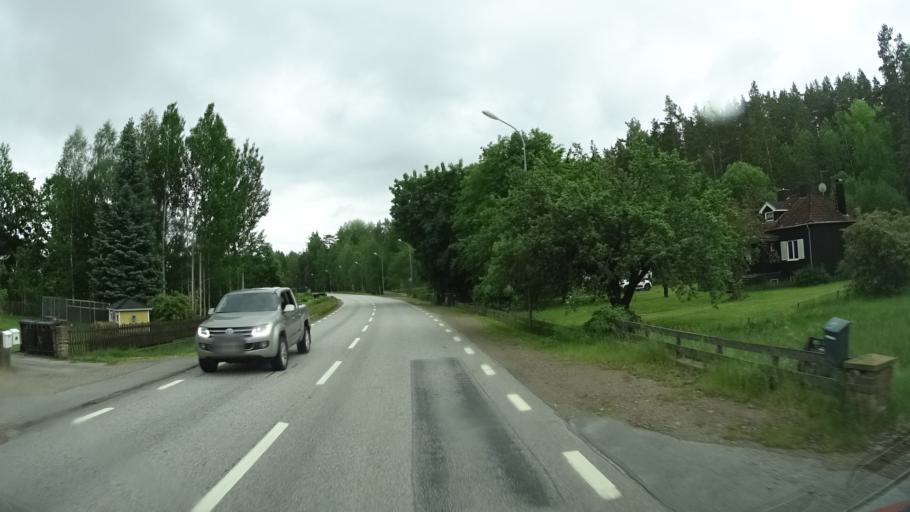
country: SE
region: Kalmar
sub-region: Hultsfreds Kommun
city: Hultsfred
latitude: 57.5362
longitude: 15.7616
